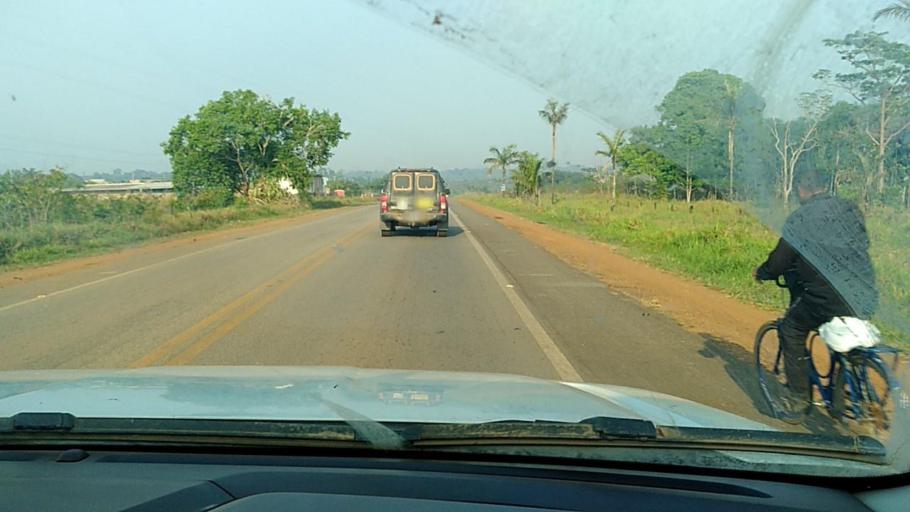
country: BR
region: Rondonia
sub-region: Porto Velho
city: Porto Velho
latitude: -8.7416
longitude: -63.9431
